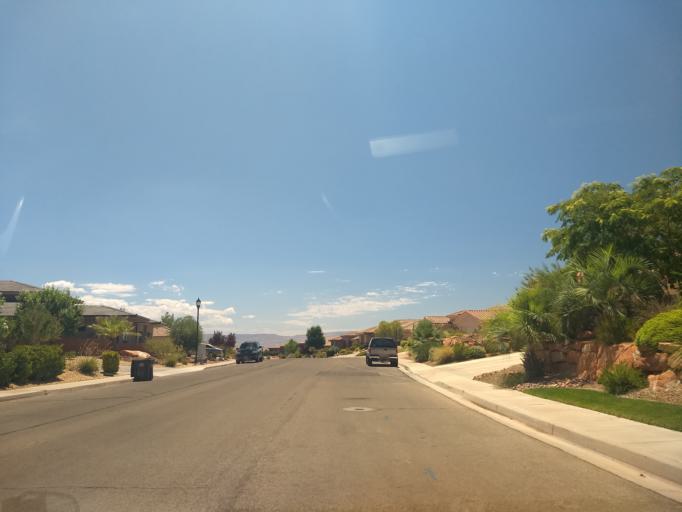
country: US
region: Utah
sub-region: Washington County
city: Washington
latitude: 37.1520
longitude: -113.5215
